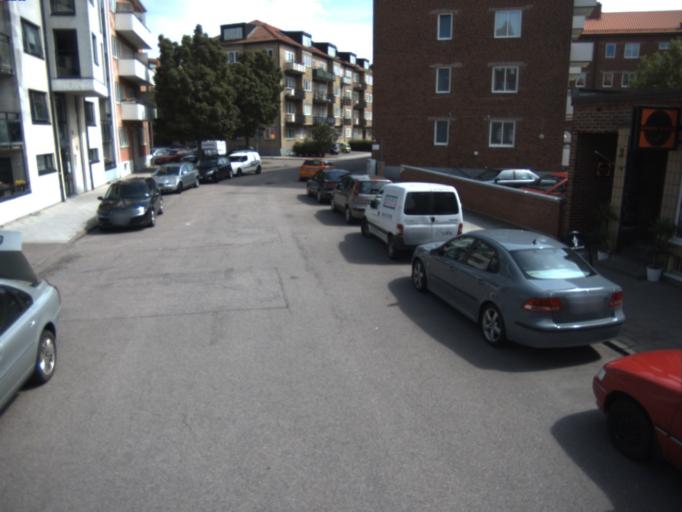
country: SE
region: Skane
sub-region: Helsingborg
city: Helsingborg
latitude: 56.0431
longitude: 12.7079
